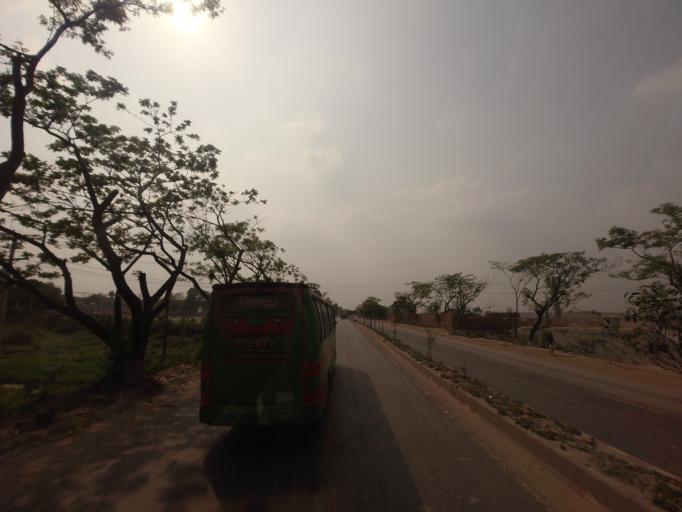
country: BD
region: Dhaka
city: Azimpur
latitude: 23.7917
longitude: 90.3051
